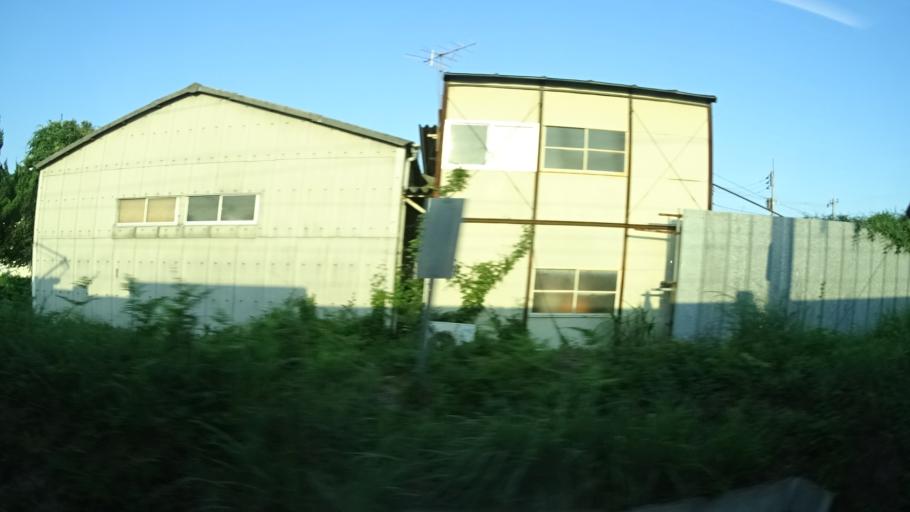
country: JP
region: Ibaraki
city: Ishioka
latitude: 36.2108
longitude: 140.2817
